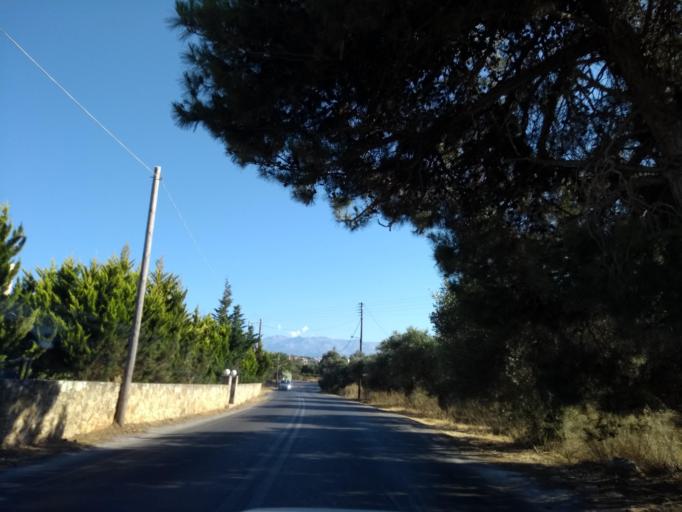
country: GR
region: Crete
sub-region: Nomos Chanias
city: Pithari
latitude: 35.5425
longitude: 24.0820
